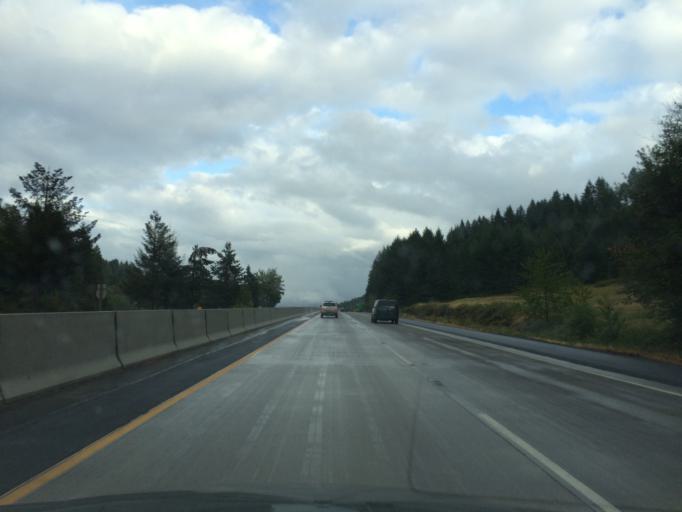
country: US
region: Oregon
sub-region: Lane County
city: Cottage Grove
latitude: 43.7533
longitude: -123.1360
